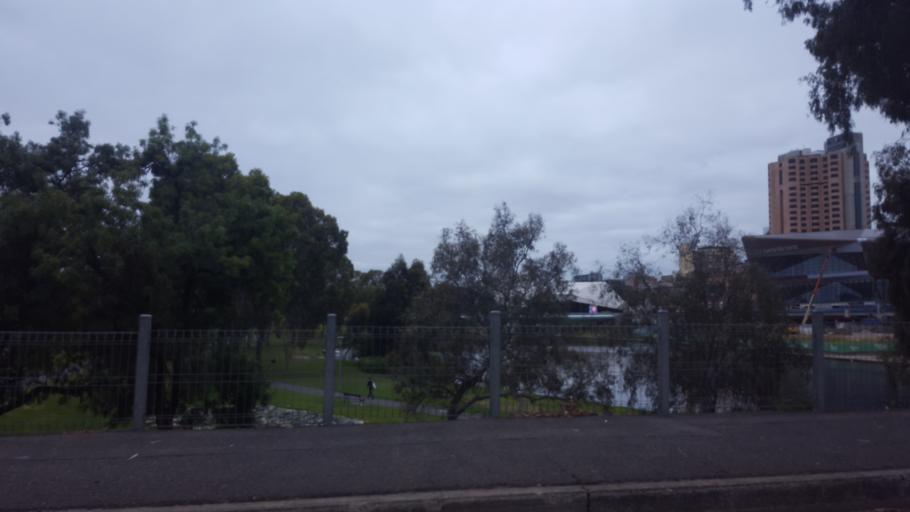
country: AU
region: South Australia
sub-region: Adelaide
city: North Adelaide
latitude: -34.9186
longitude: 138.5932
